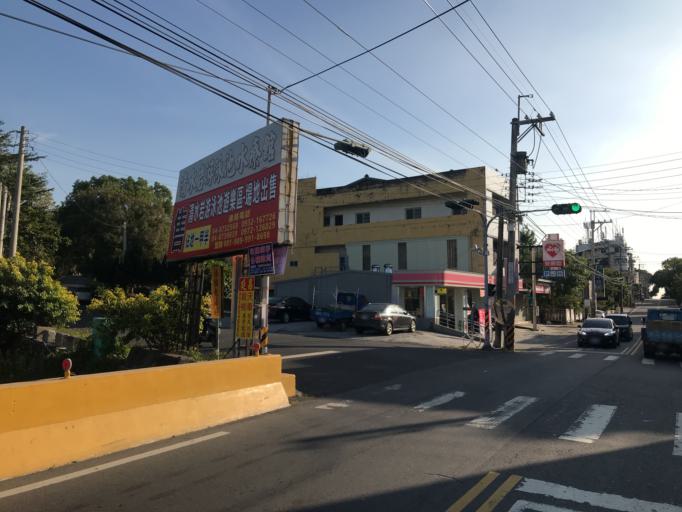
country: TW
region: Taiwan
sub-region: Nantou
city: Nantou
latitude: 23.8891
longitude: 120.6095
